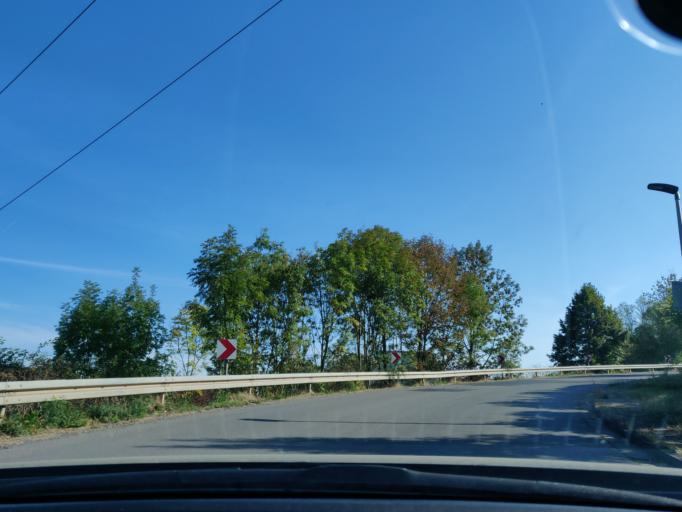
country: DE
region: Hesse
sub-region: Regierungsbezirk Kassel
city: Bad Wildungen
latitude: 51.1196
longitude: 9.1514
